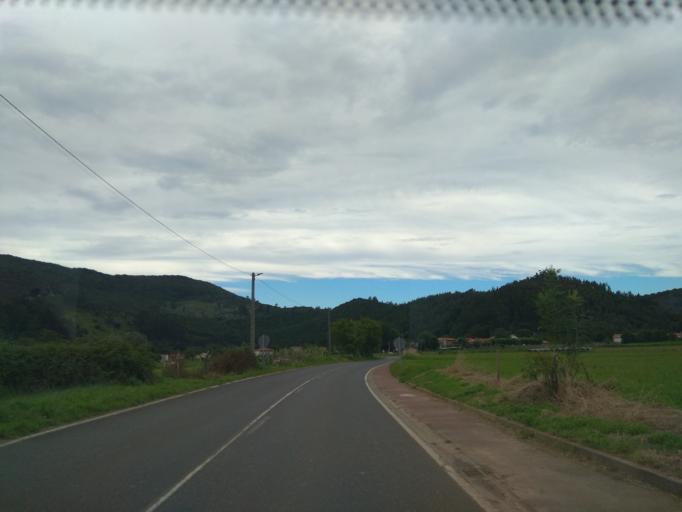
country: ES
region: Cantabria
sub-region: Provincia de Cantabria
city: Hazas de Cesto
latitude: 43.3969
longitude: -3.5940
